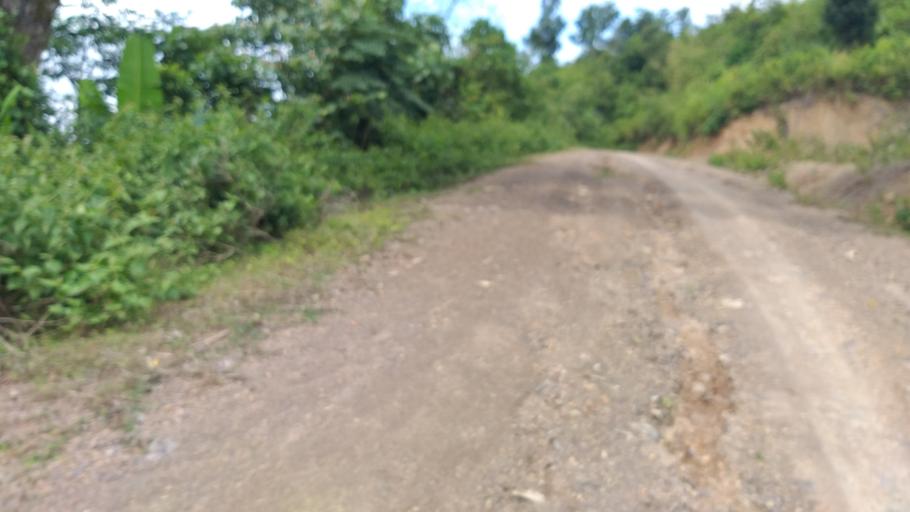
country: VN
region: Huyen Dien Bien
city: Dien Bien Phu
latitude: 21.4704
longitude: 102.6807
